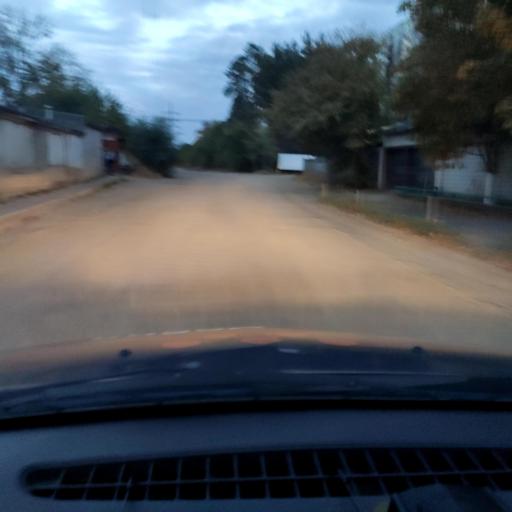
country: RU
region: Voronezj
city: Pridonskoy
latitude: 51.6882
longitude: 39.0794
